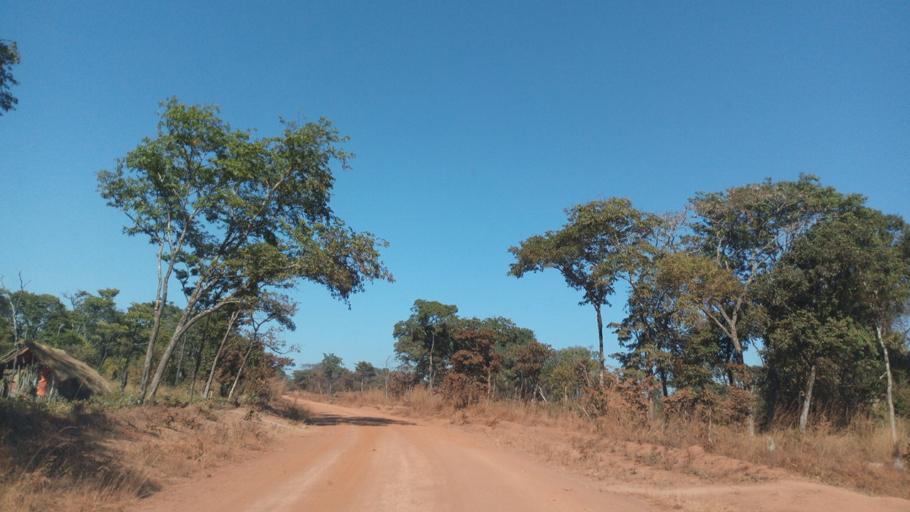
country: ZM
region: Luapula
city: Mwense
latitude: -10.7098
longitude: 28.3664
